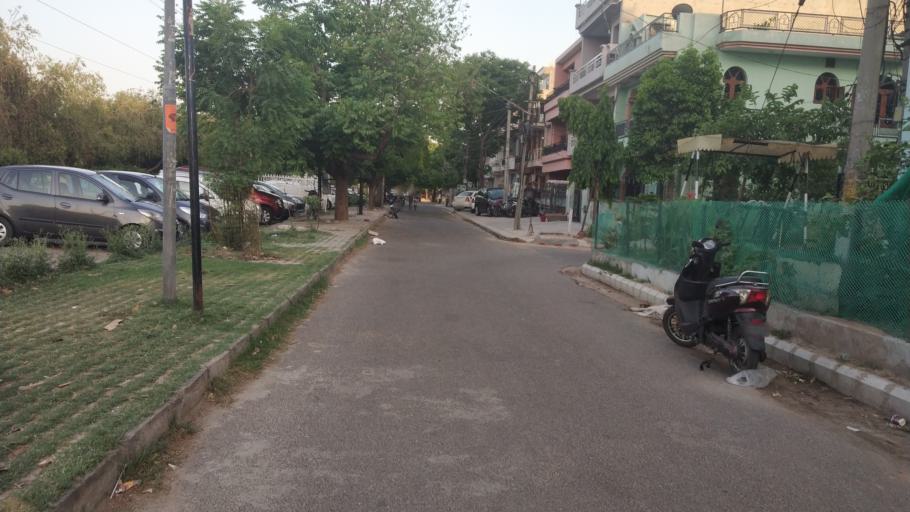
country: IN
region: Punjab
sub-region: Ajitgarh
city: Mohali
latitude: 30.6865
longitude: 76.7300
